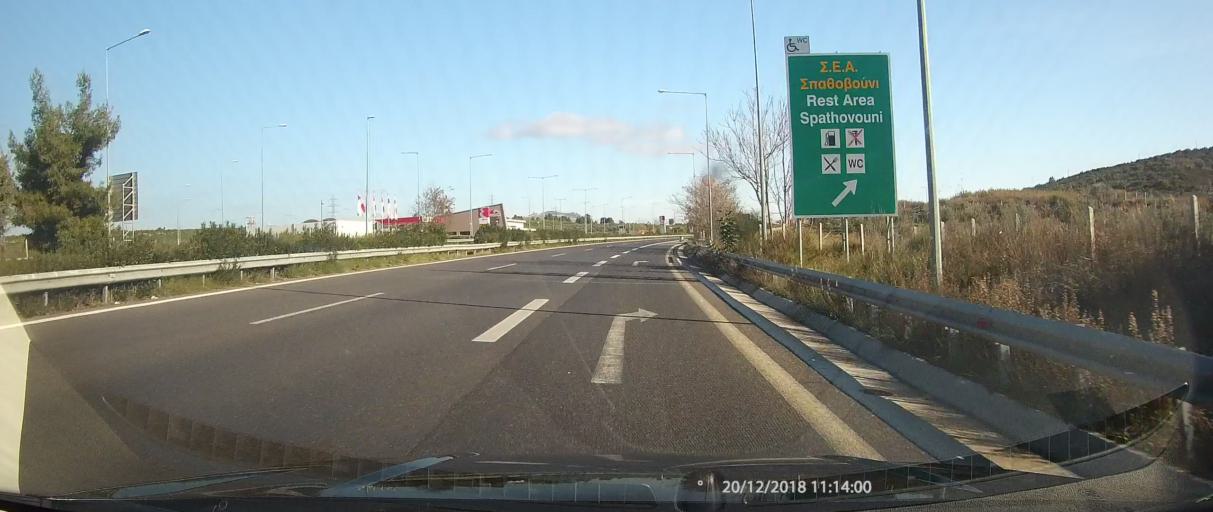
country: GR
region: Peloponnese
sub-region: Nomos Korinthias
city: Khiliomodhi
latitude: 37.8613
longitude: 22.8385
